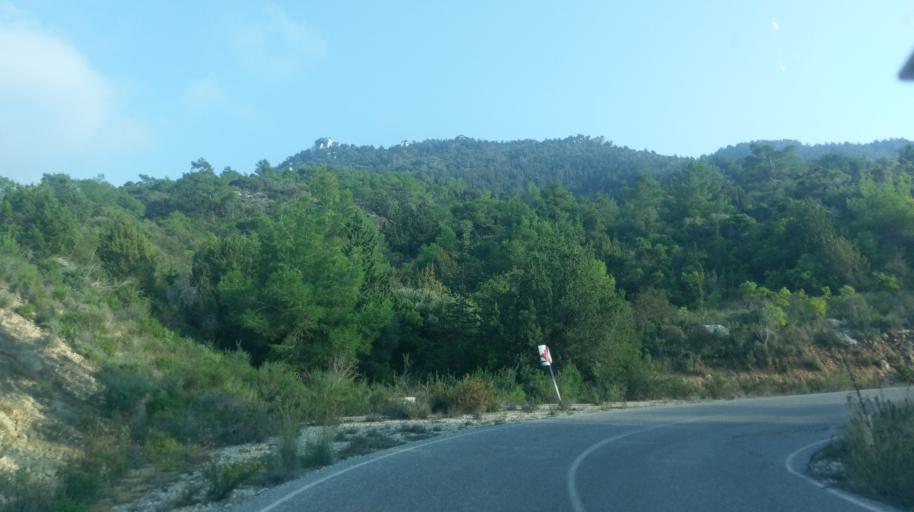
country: CY
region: Ammochostos
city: Trikomo
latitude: 35.4065
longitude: 33.9045
